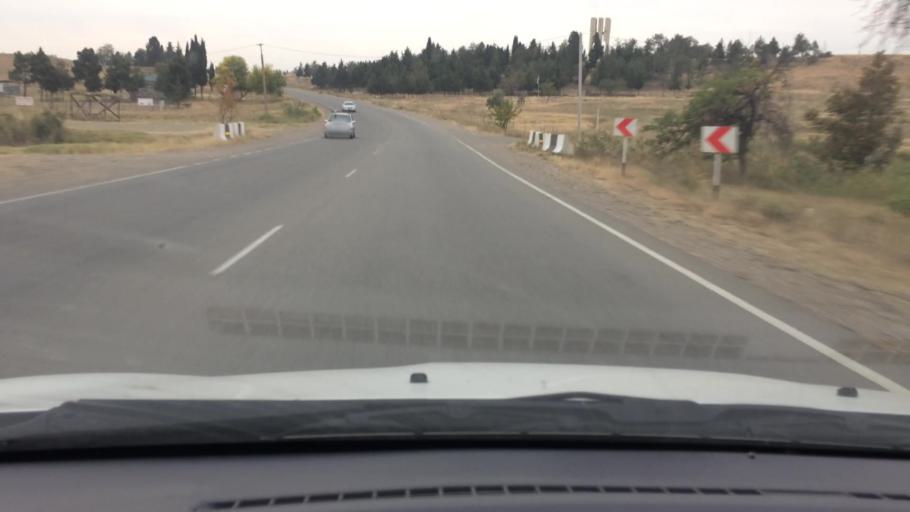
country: GE
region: Kvemo Kartli
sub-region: Marneuli
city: Marneuli
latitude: 41.5270
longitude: 44.7770
